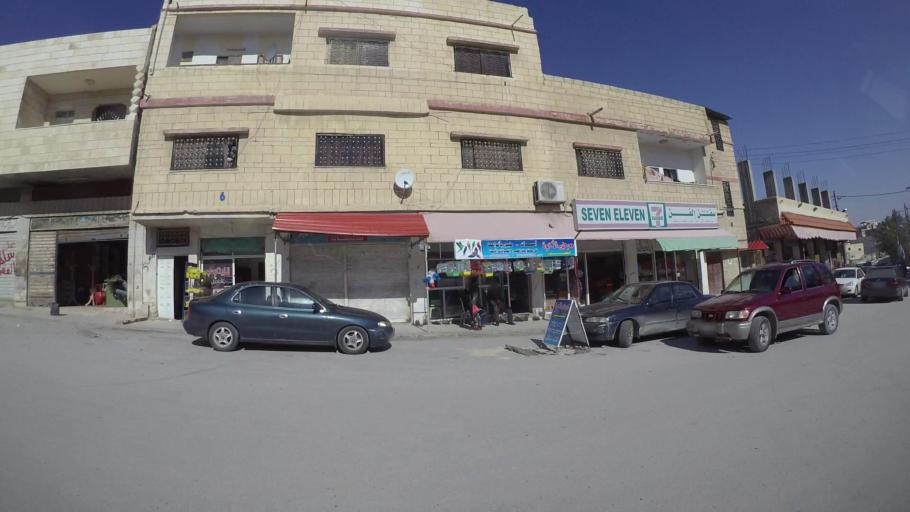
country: JO
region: Zarqa
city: Russeifa
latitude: 32.0328
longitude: 36.0380
